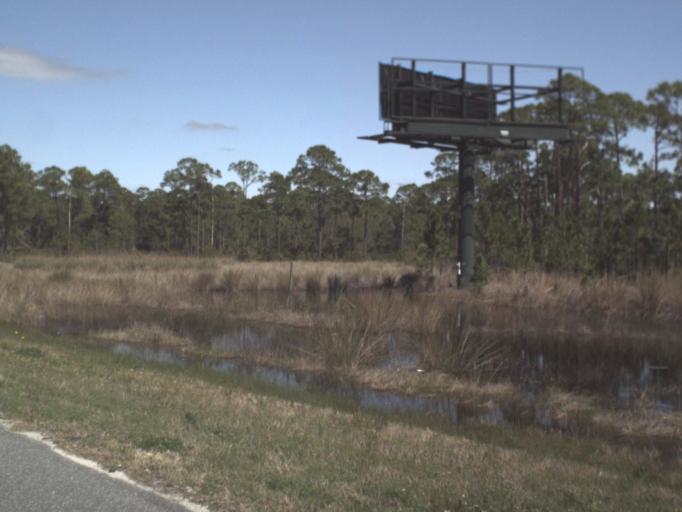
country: US
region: Florida
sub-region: Wakulla County
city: Crawfordville
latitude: 29.9816
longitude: -84.3837
